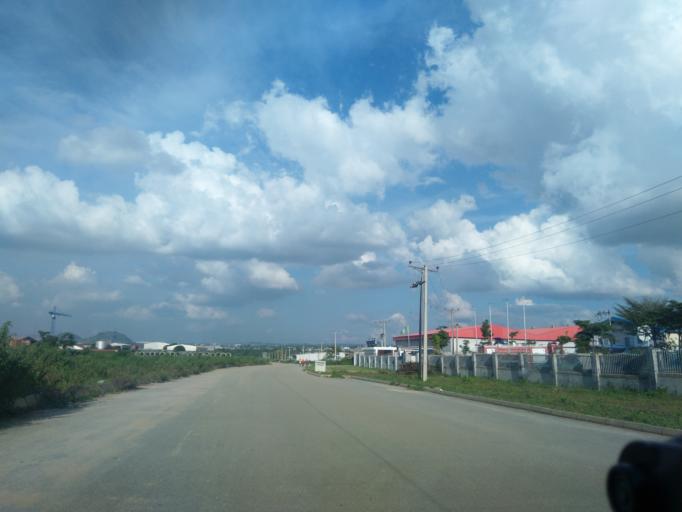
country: NG
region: Abuja Federal Capital Territory
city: Abuja
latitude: 9.0296
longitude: 7.4029
